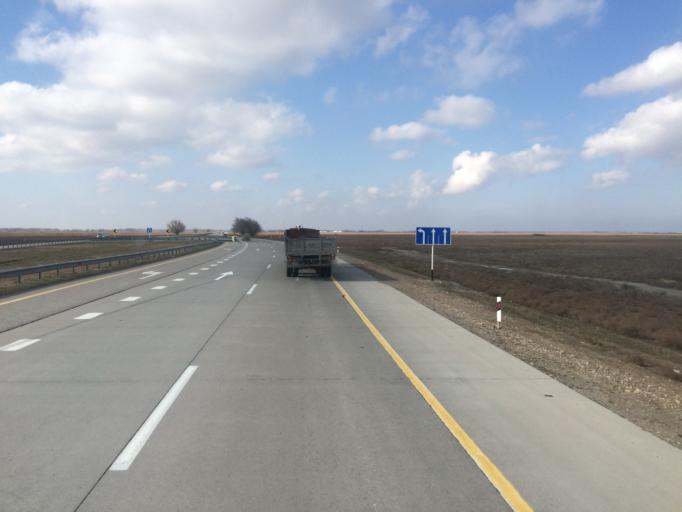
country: KZ
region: Ongtustik Qazaqstan
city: Temirlanovka
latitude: 42.8712
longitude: 69.0525
